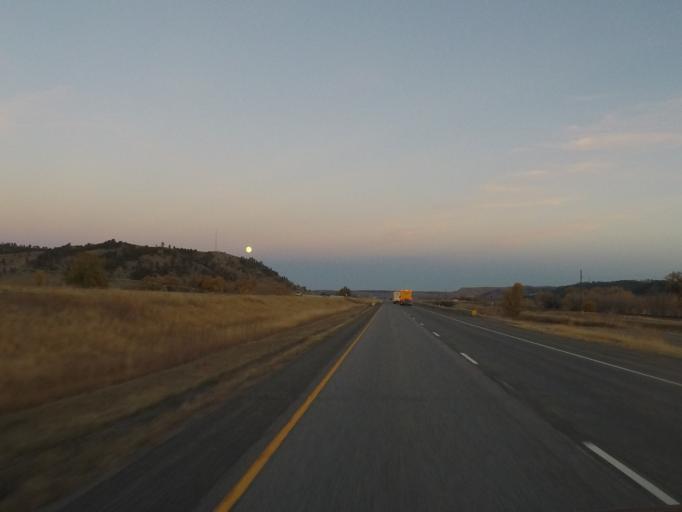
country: US
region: Montana
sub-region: Stillwater County
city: Columbus
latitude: 45.6057
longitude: -109.1611
